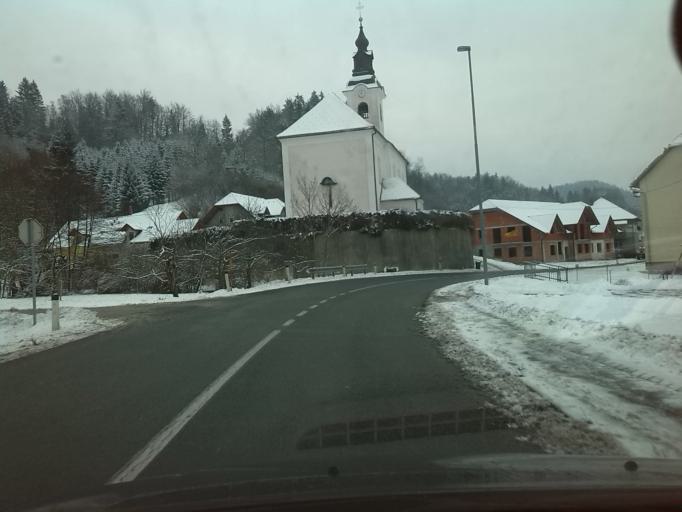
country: SI
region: Lukovica
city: Lukovica pri Domzalah
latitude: 46.2244
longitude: 14.6919
